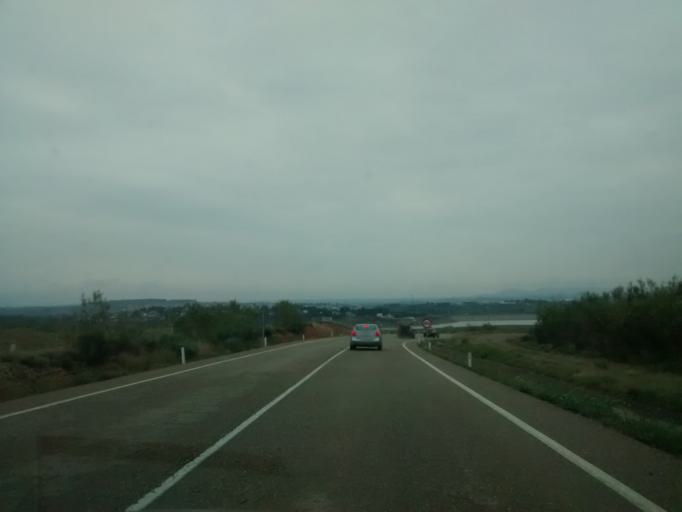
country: ES
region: Aragon
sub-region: Provincia de Zaragoza
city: Caspe
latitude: 41.2618
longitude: -0.0550
